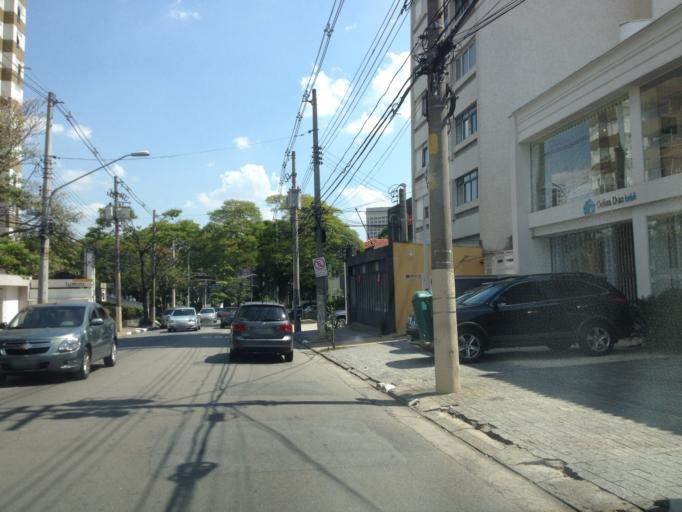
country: BR
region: Sao Paulo
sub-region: Sao Paulo
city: Sao Paulo
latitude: -23.5717
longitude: -46.6813
